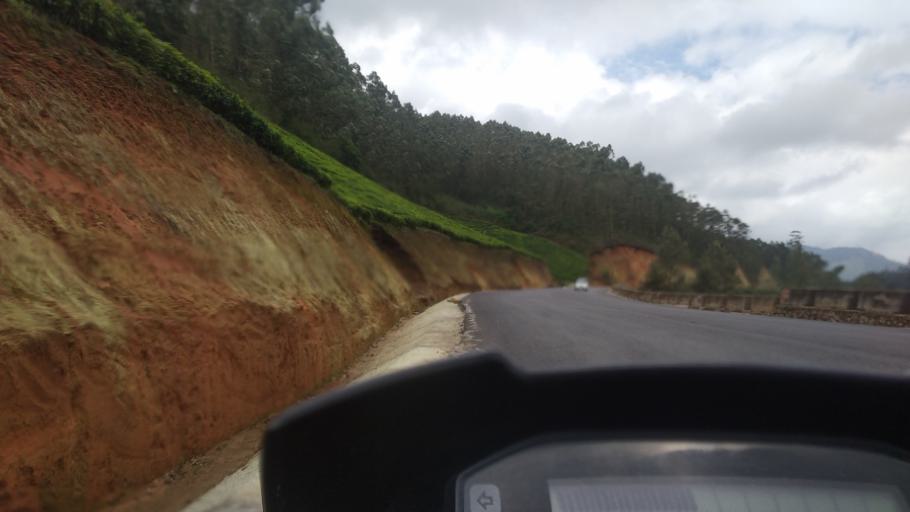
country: IN
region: Kerala
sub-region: Idukki
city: Munnar
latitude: 10.0764
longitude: 77.0875
